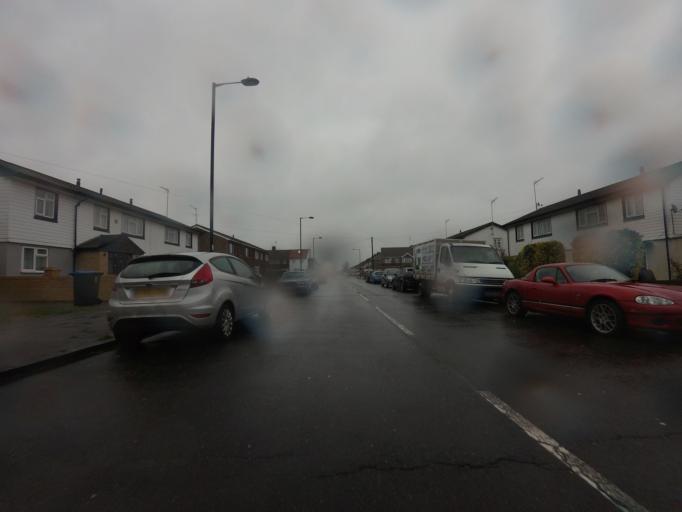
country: GB
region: England
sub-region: Hertfordshire
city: Waltham Cross
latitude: 51.6669
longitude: -0.0270
